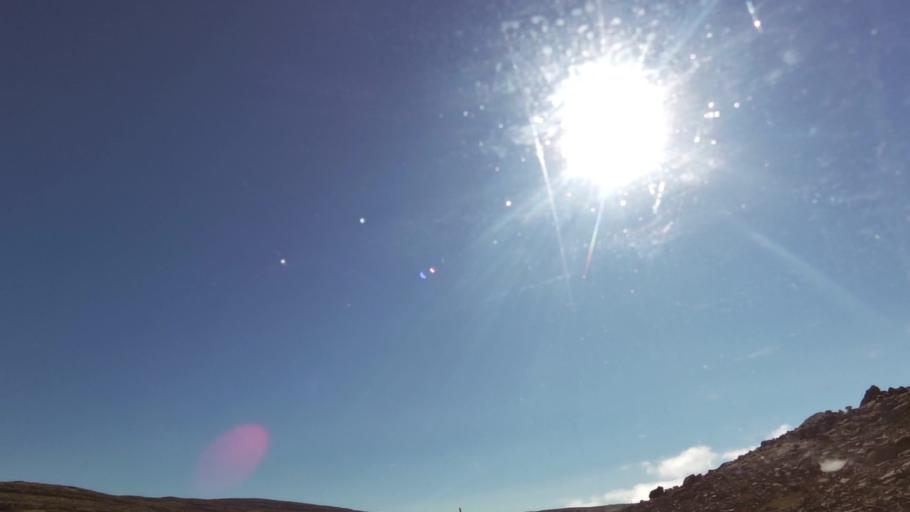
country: IS
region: West
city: Olafsvik
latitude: 65.5508
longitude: -24.2056
